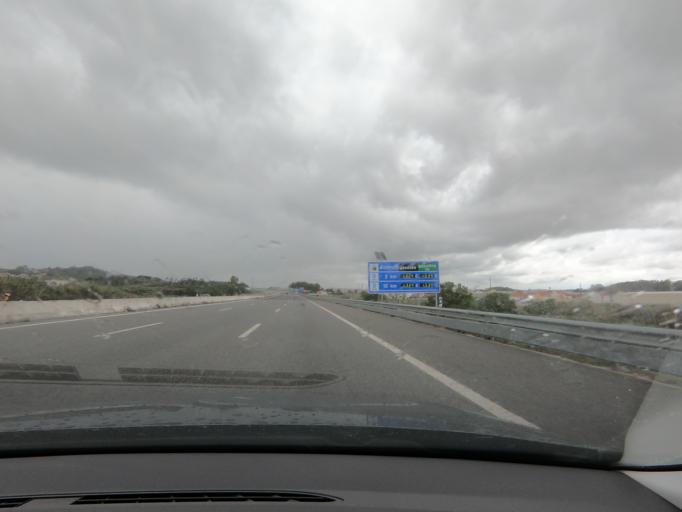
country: PT
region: Lisbon
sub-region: Sintra
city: Sintra
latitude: 38.7728
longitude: -9.3674
